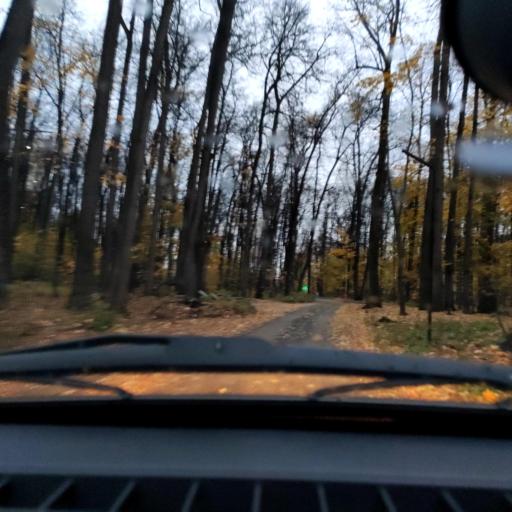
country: RU
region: Bashkortostan
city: Ufa
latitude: 54.7676
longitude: 56.0075
